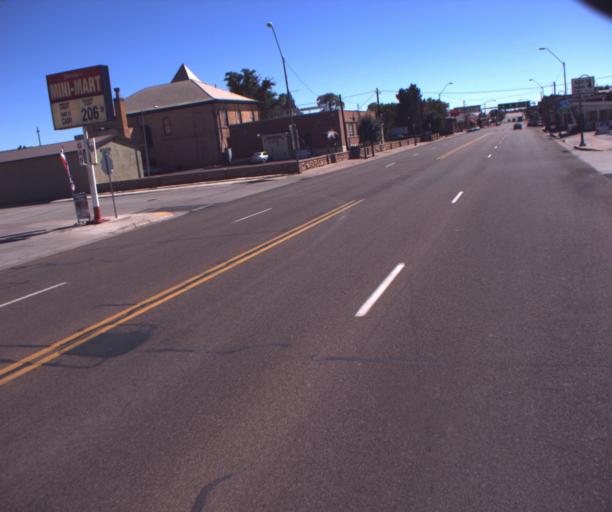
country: US
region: Arizona
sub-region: Navajo County
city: Holbrook
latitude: 34.9041
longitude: -110.1582
